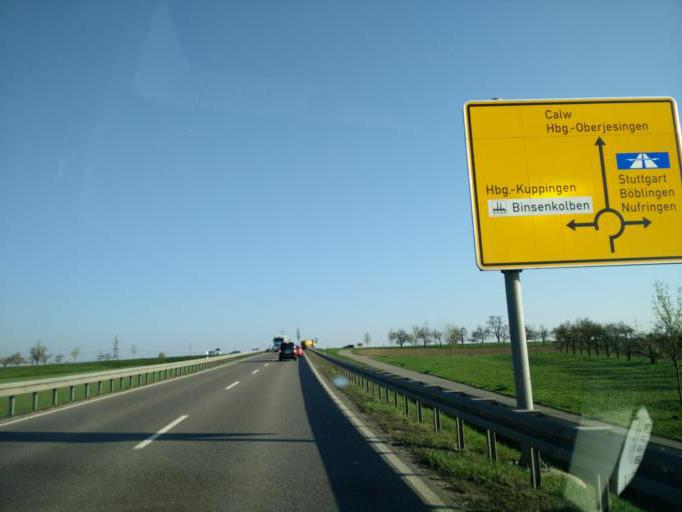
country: DE
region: Baden-Wuerttemberg
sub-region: Regierungsbezirk Stuttgart
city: Herrenberg
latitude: 48.6131
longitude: 8.8529
